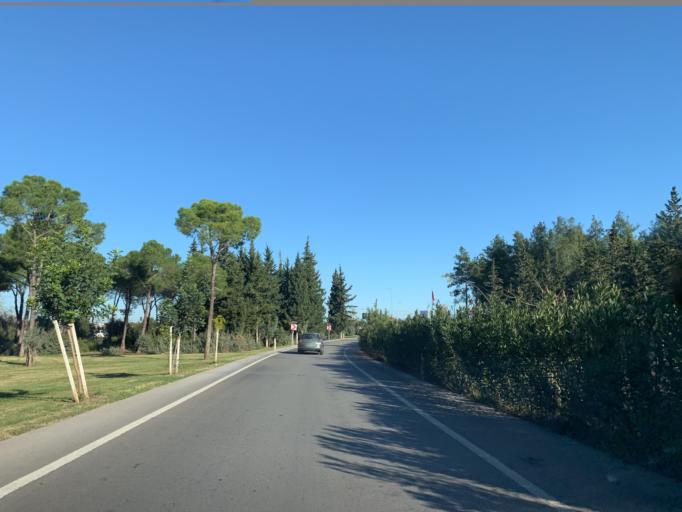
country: TR
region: Antalya
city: Aksu
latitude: 36.9310
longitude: 30.8087
